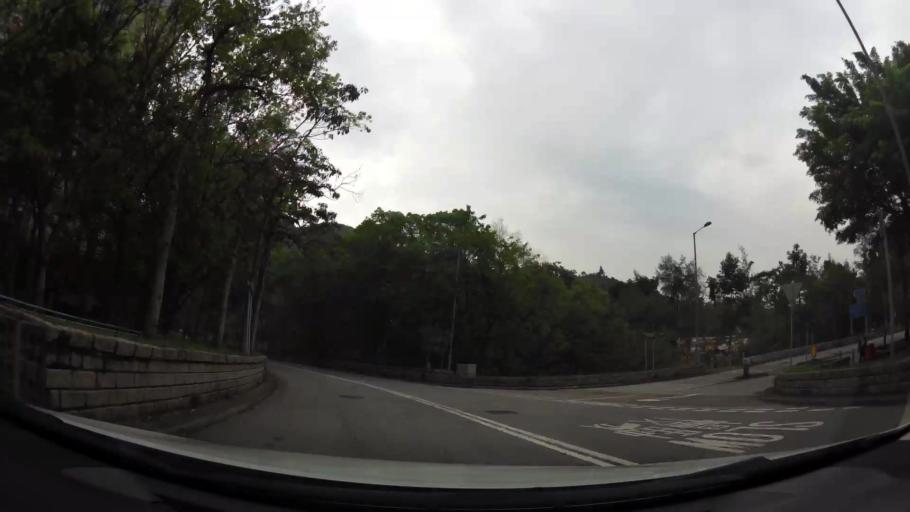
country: HK
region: Tai Po
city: Tai Po
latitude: 22.4609
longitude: 114.1730
